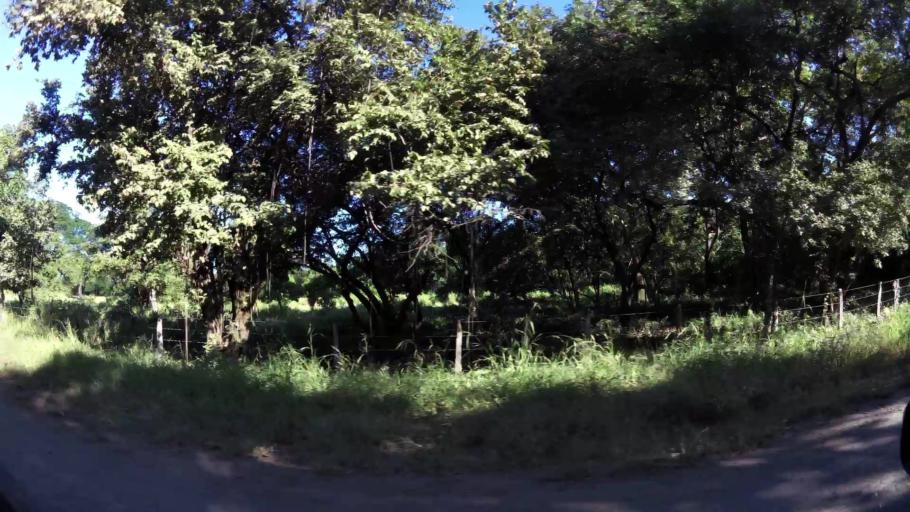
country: CR
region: Guanacaste
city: Sardinal
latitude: 10.4856
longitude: -85.5811
